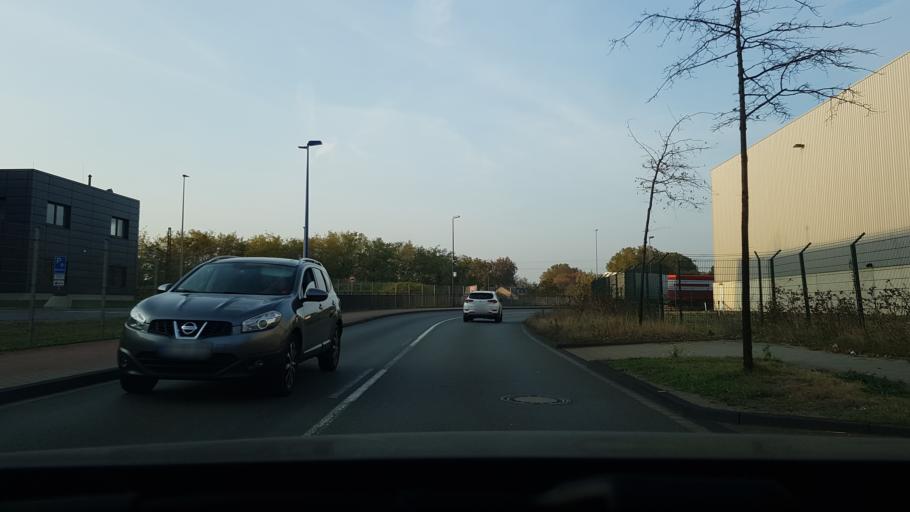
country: DE
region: North Rhine-Westphalia
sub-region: Regierungsbezirk Dusseldorf
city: Hochfeld
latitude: 51.4021
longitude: 6.7275
